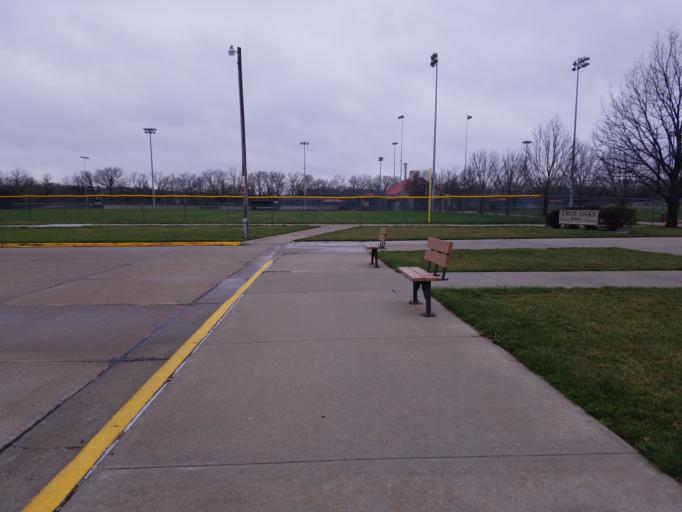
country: US
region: Kansas
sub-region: Riley County
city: Manhattan
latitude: 39.1870
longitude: -96.6322
